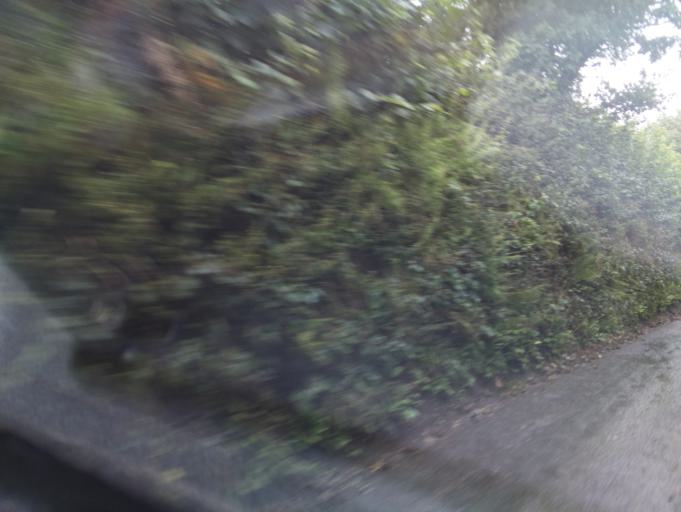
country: GB
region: England
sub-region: Devon
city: Totnes
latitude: 50.3434
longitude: -3.6842
